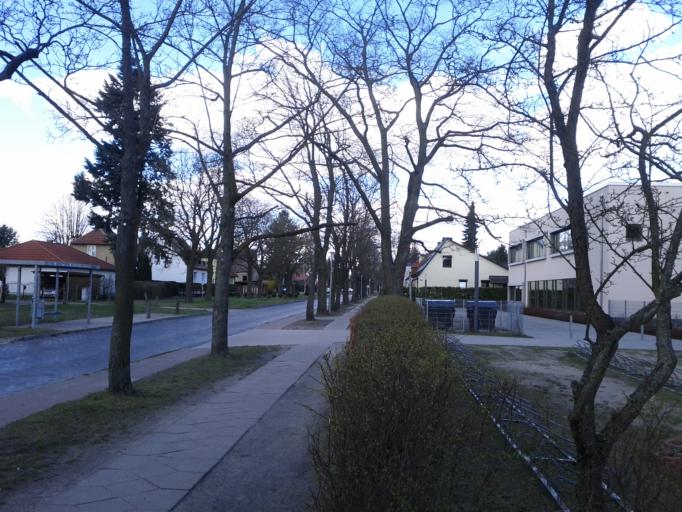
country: DE
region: Brandenburg
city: Woltersdorf
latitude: 52.4540
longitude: 13.7527
